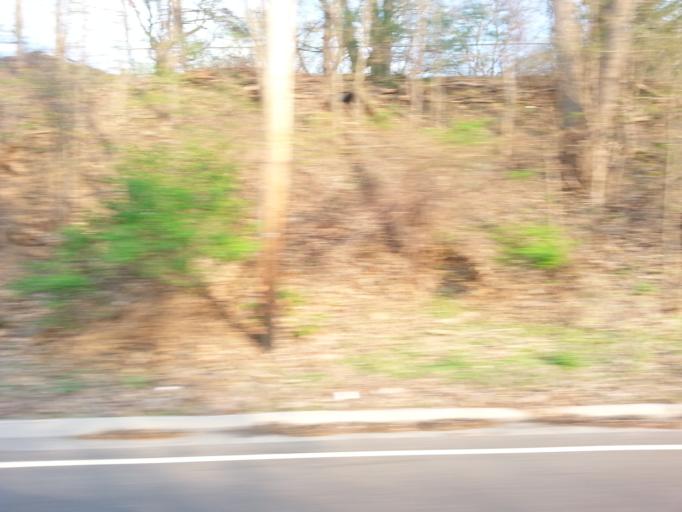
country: US
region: Minnesota
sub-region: Dakota County
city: West Saint Paul
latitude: 44.9126
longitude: -93.1189
